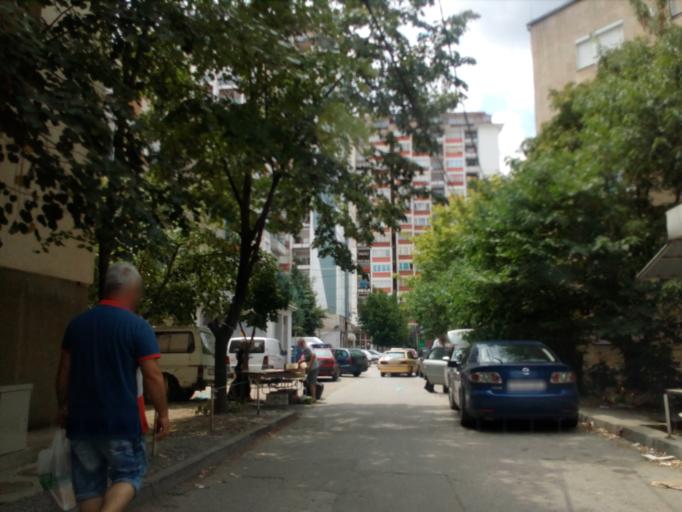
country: MK
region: Veles
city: Veles
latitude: 41.7148
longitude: 21.7668
